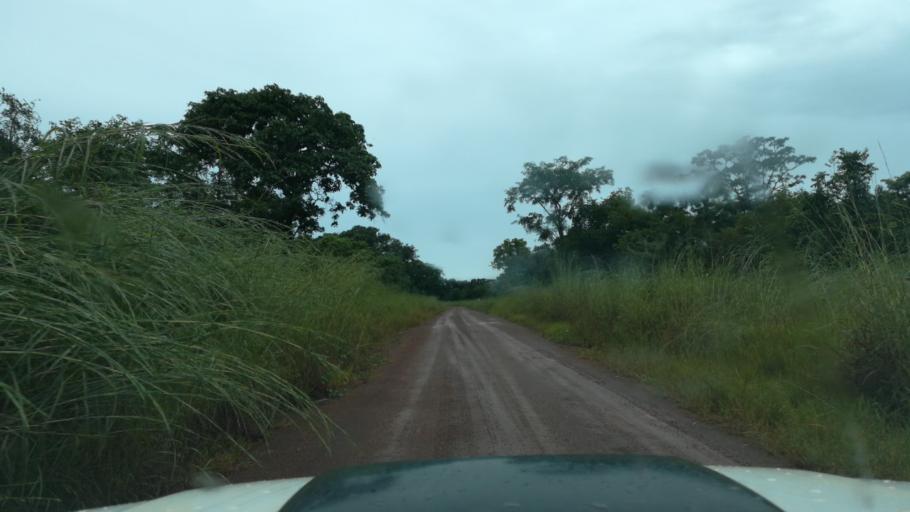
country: ZM
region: Luapula
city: Mwense
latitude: -10.3186
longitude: 28.1125
